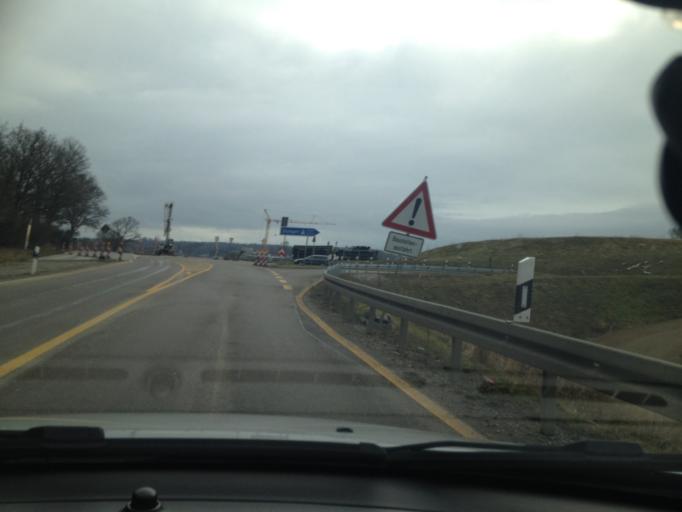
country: DE
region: Bavaria
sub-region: Swabia
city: Zusmarshausen
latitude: 48.4120
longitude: 10.5990
